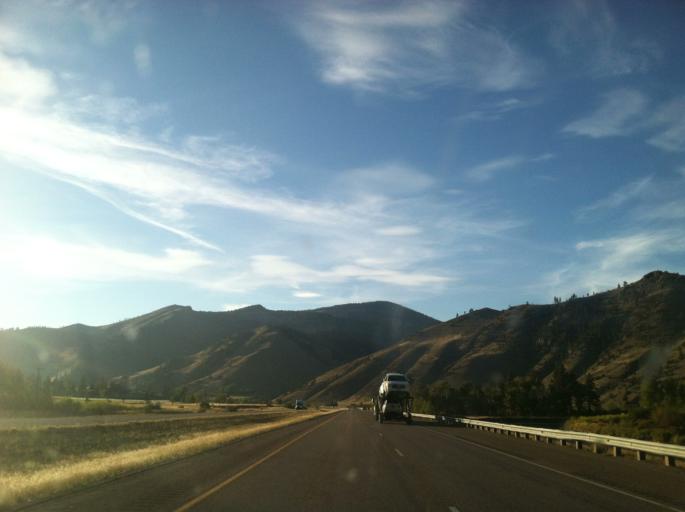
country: US
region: Montana
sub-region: Missoula County
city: Clinton
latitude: 46.6999
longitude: -113.3625
